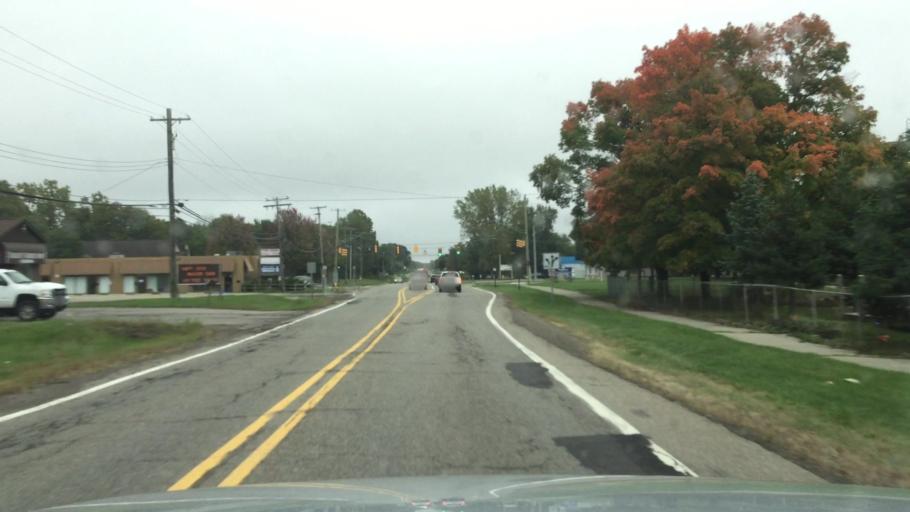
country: US
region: Michigan
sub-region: Oakland County
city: Waterford
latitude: 42.6758
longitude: -83.4067
